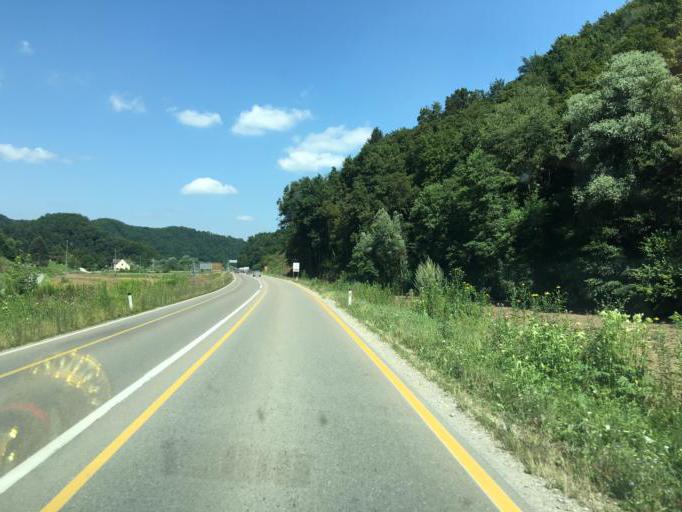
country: SI
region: Zetale
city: Zetale
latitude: 46.2902
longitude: 15.8569
